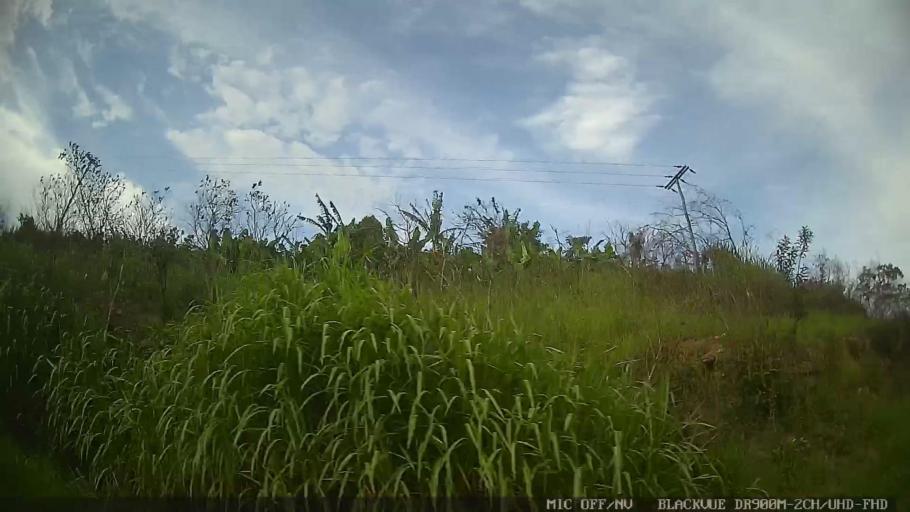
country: BR
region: Sao Paulo
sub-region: Amparo
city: Amparo
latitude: -22.6923
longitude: -46.7276
